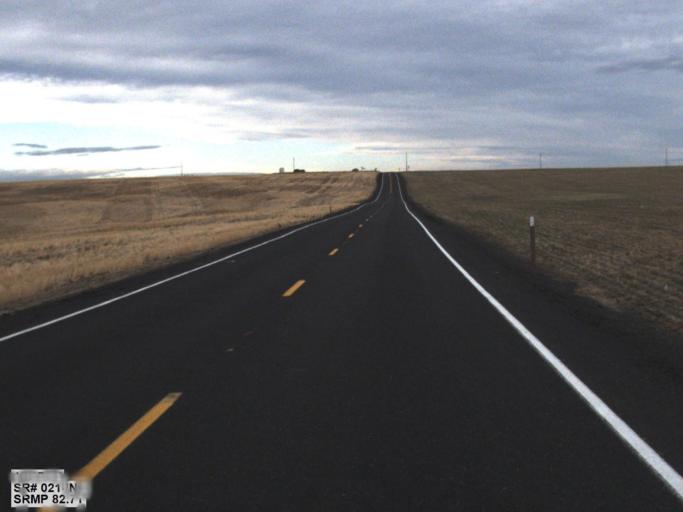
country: US
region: Washington
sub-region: Okanogan County
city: Coulee Dam
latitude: 47.6358
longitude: -118.7208
